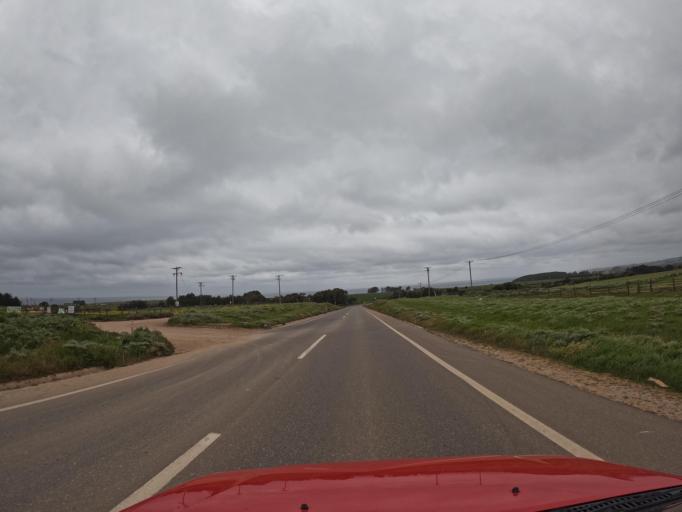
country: CL
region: O'Higgins
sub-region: Provincia de Colchagua
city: Santa Cruz
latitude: -34.4905
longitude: -72.0165
